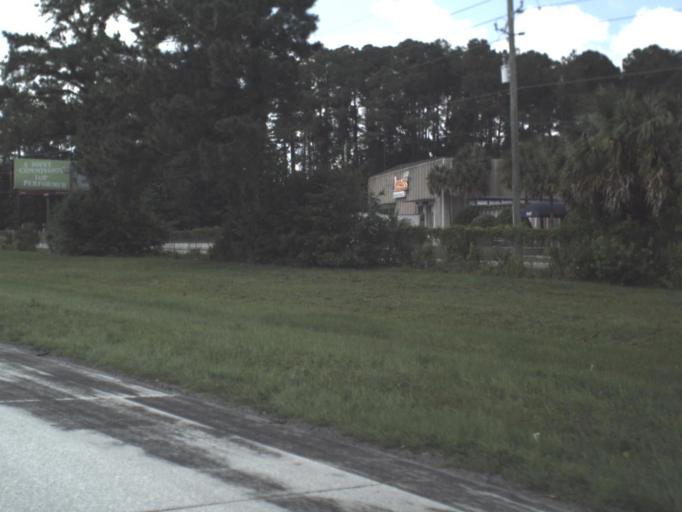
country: US
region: Florida
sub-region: Duval County
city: Jacksonville
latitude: 30.2354
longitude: -81.5806
